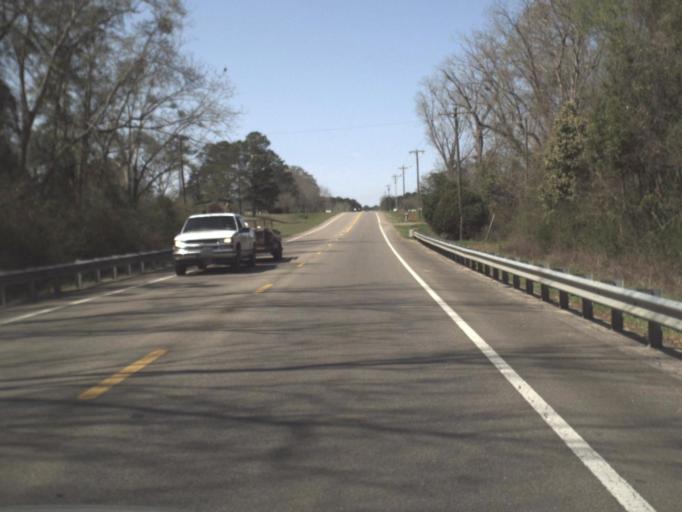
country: US
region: Florida
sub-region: Gadsden County
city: Gretna
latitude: 30.5917
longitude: -84.6509
